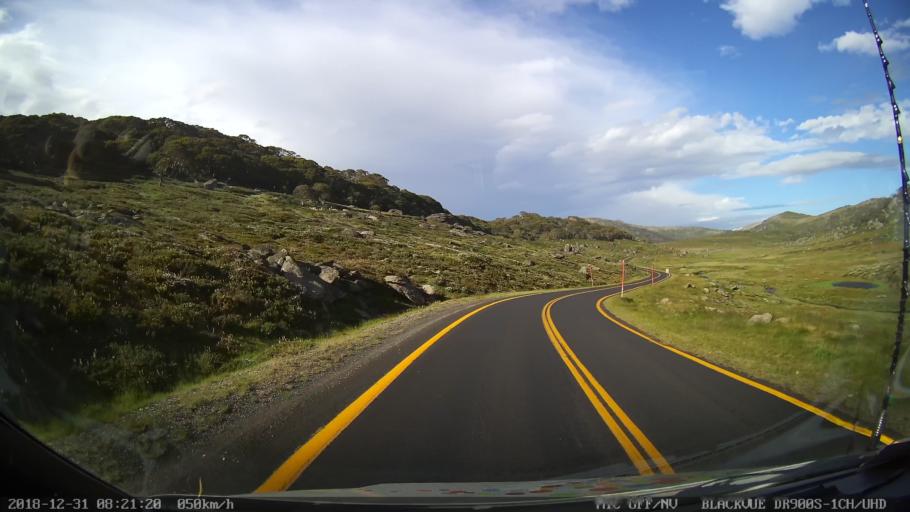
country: AU
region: New South Wales
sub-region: Snowy River
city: Jindabyne
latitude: -36.4271
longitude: 148.3686
